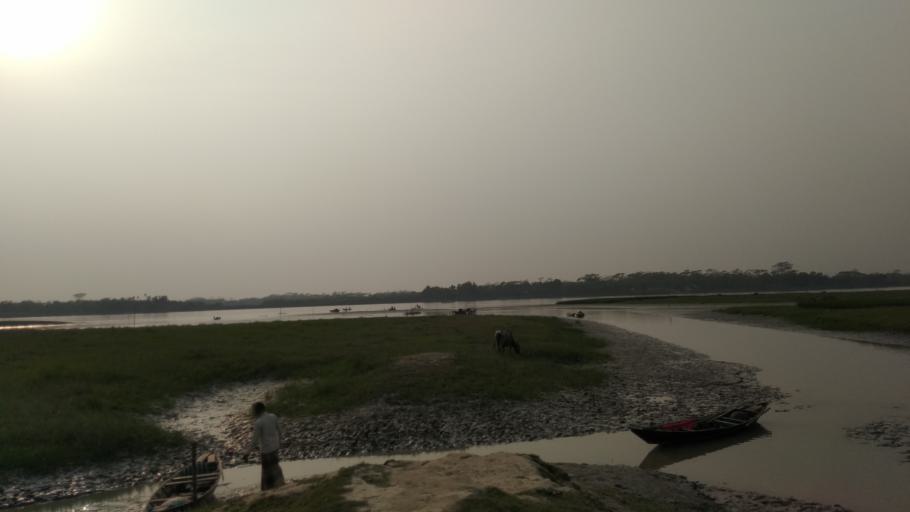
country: BD
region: Barisal
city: Mehendiganj
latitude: 22.9107
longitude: 90.3968
